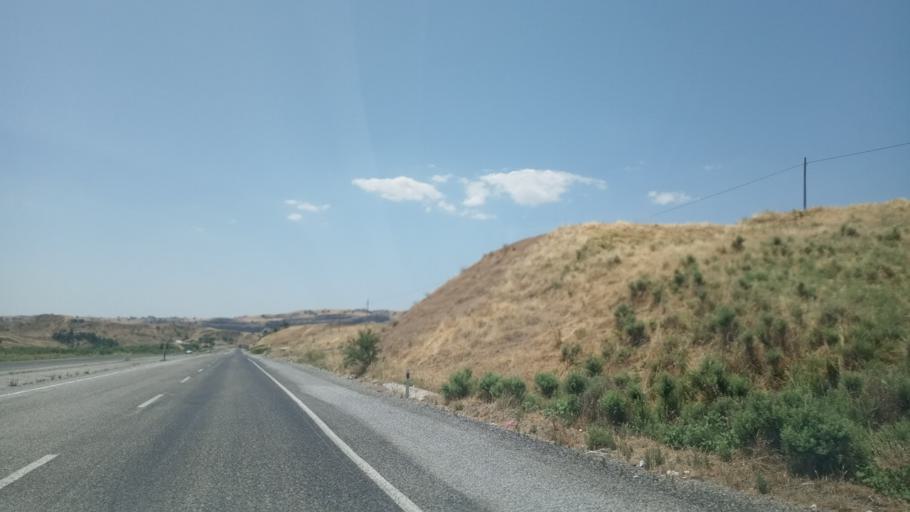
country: TR
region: Batman
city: Kozluk
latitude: 38.1566
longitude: 41.4137
